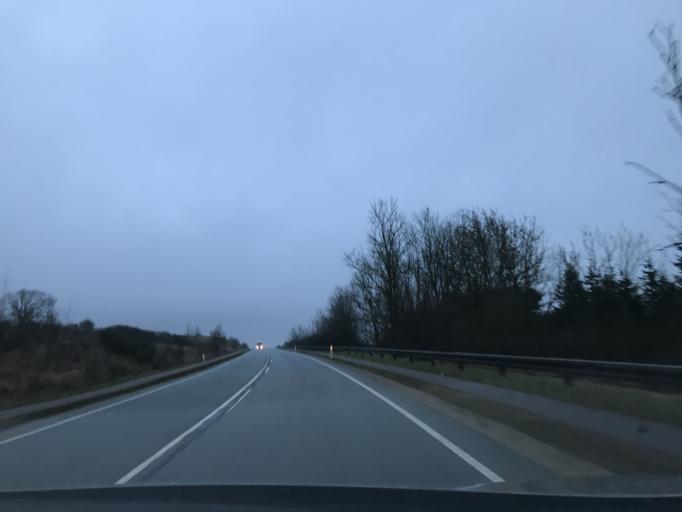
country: DK
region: Central Jutland
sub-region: Hedensted Kommune
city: Hedensted
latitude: 55.7069
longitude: 9.7503
